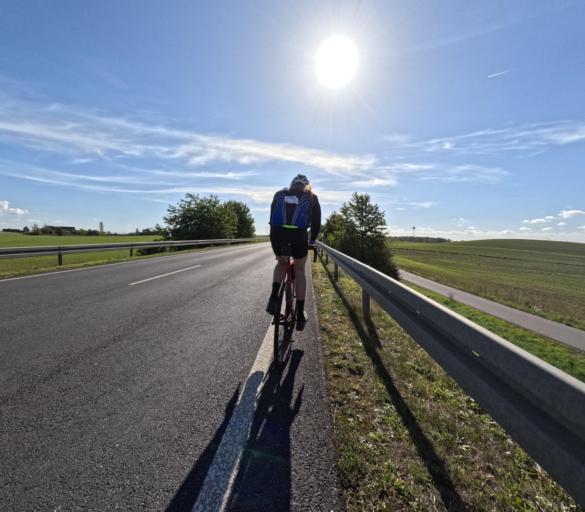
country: DE
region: Saxony
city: Moritzburg
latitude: 51.1432
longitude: 13.6510
